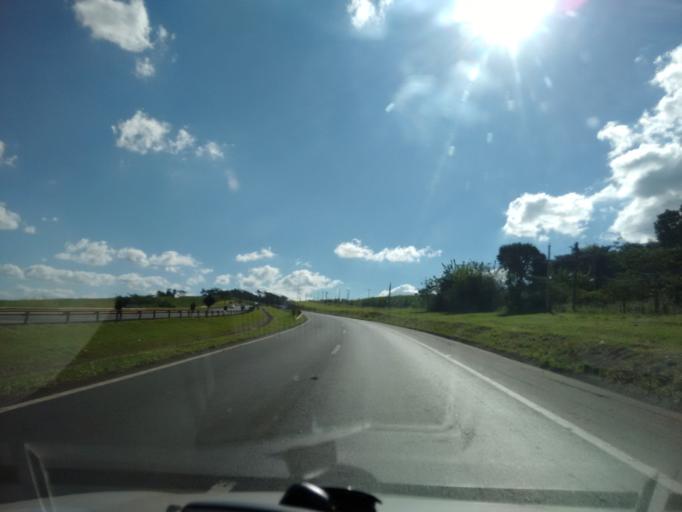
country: BR
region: Sao Paulo
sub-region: Araraquara
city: Araraquara
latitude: -21.8766
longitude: -48.0934
